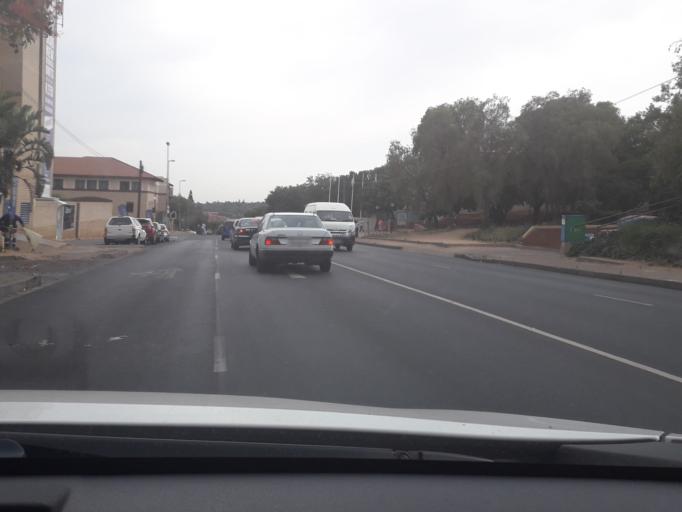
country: ZA
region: Gauteng
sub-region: City of Johannesburg Metropolitan Municipality
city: Johannesburg
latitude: -26.0936
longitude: 28.0003
